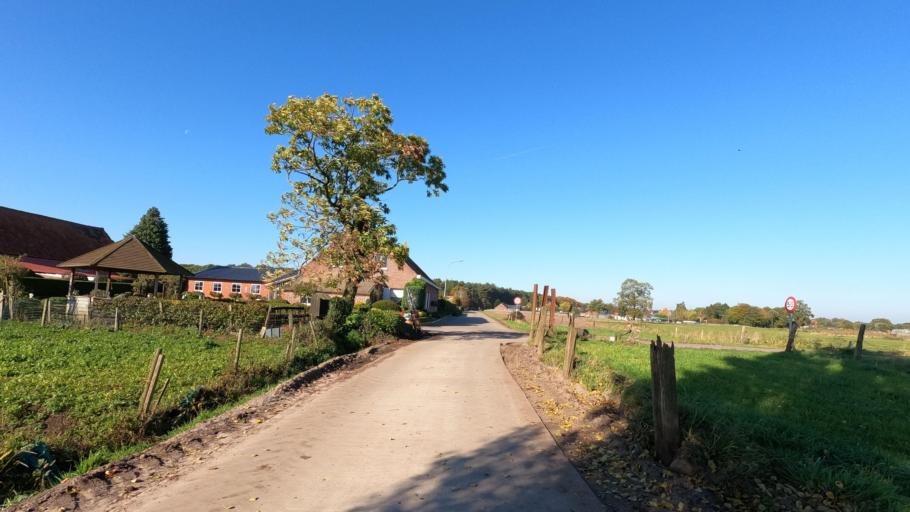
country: BE
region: Flanders
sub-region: Provincie Antwerpen
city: Merksplas
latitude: 51.3485
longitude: 4.8480
